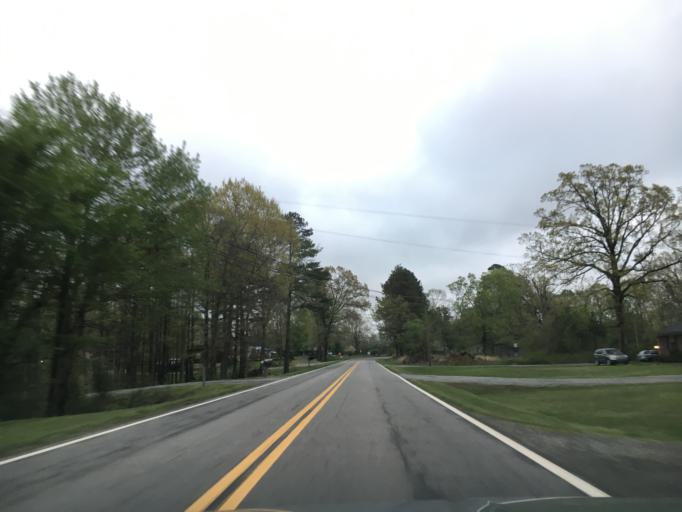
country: US
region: Virginia
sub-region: Halifax County
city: South Boston
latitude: 36.6721
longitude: -78.8855
